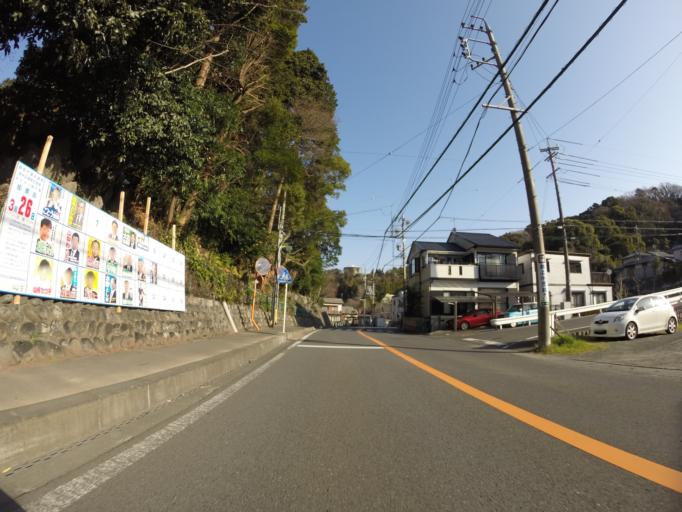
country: JP
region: Shizuoka
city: Shizuoka-shi
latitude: 34.9944
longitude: 138.4533
